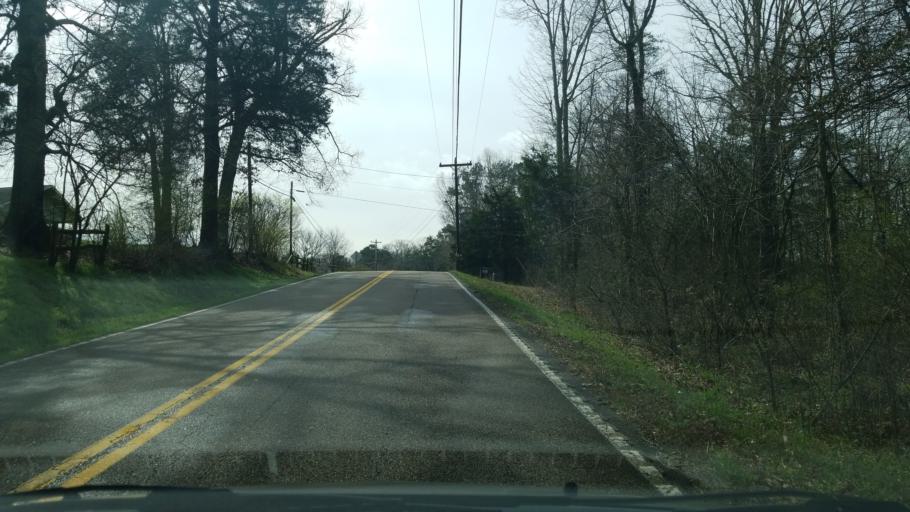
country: US
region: Tennessee
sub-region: Hamilton County
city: Harrison
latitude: 35.1237
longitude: -85.0697
